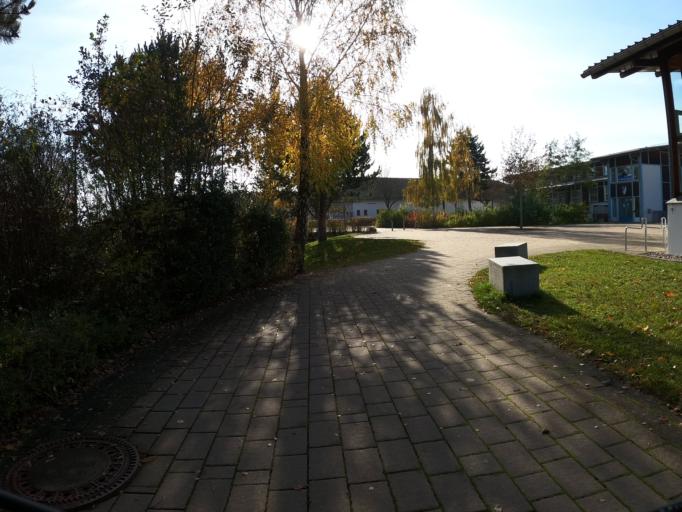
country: DE
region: Bavaria
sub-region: Swabia
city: Nersingen
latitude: 48.4500
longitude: 10.0965
